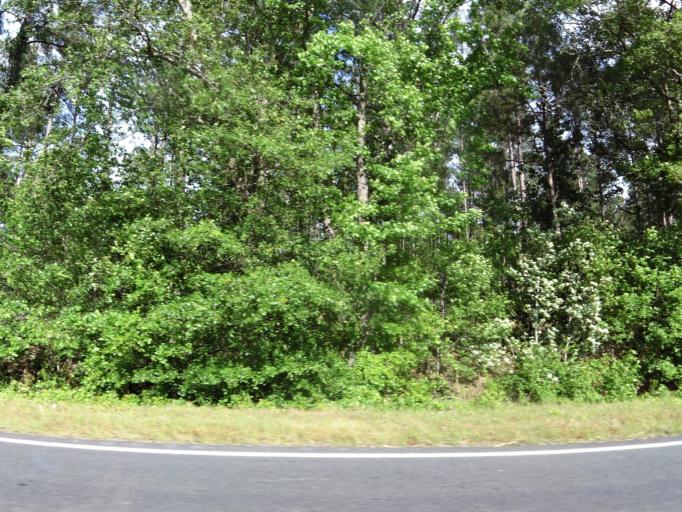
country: US
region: South Carolina
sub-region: Allendale County
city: Fairfax
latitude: 33.0070
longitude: -81.2185
